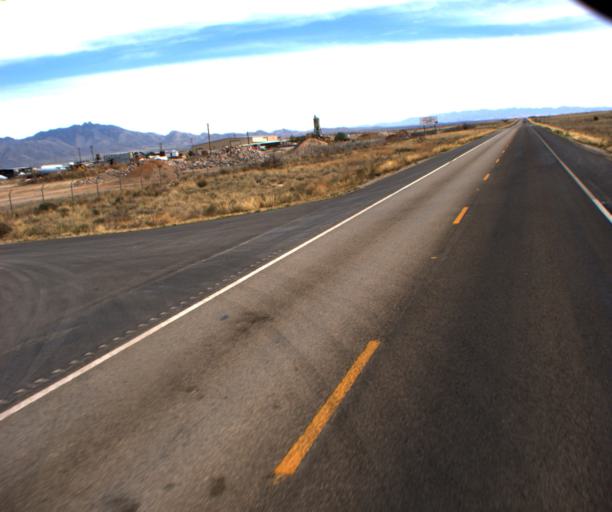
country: US
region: Arizona
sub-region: Cochise County
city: Willcox
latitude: 32.2409
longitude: -109.8136
